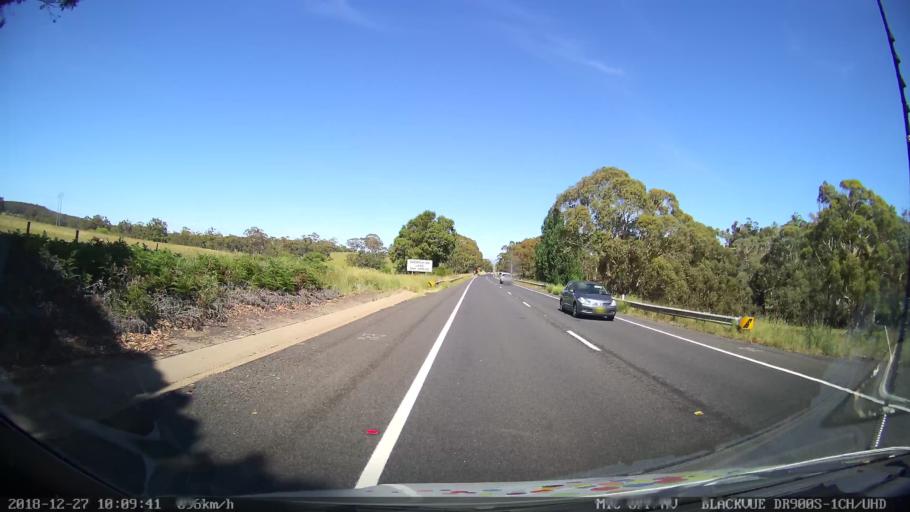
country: AU
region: New South Wales
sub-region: Lithgow
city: Portland
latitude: -33.4516
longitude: 149.8046
